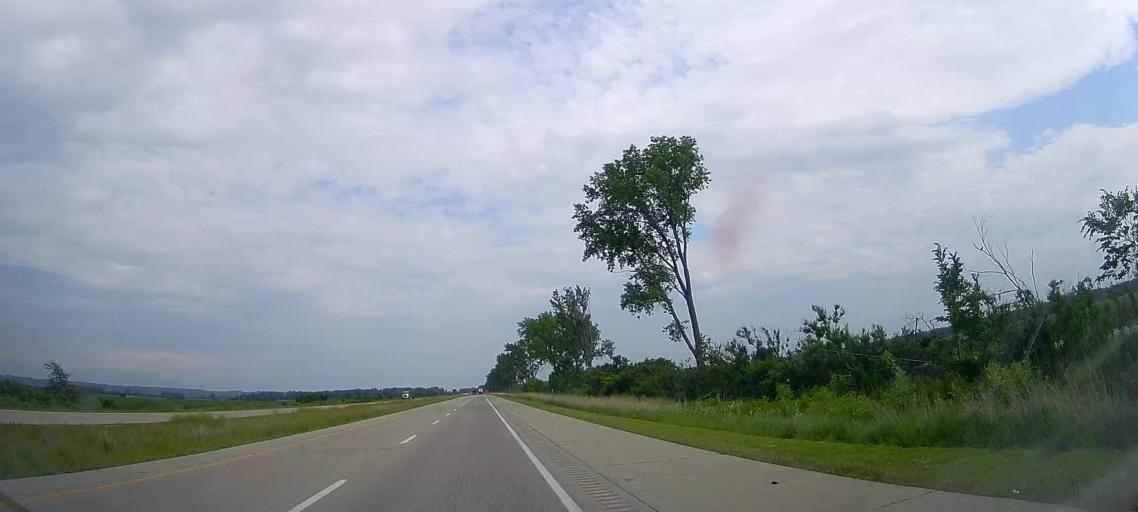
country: US
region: Nebraska
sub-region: Burt County
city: Tekamah
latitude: 41.8353
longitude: -96.0845
